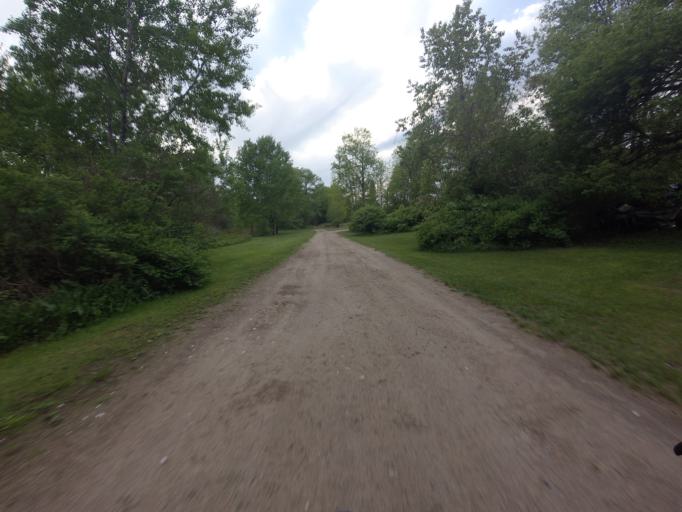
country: US
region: New York
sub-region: St. Lawrence County
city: Gouverneur
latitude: 44.1535
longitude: -75.3271
